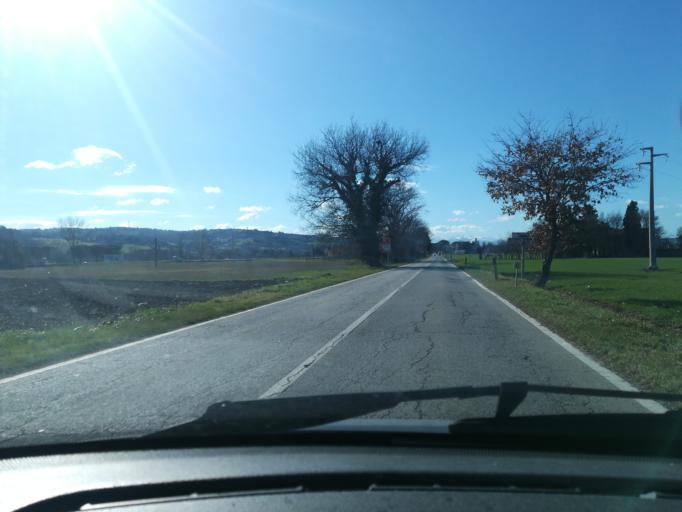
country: IT
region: The Marches
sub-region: Provincia di Macerata
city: Villa Potenza
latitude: 43.3345
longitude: 13.4272
